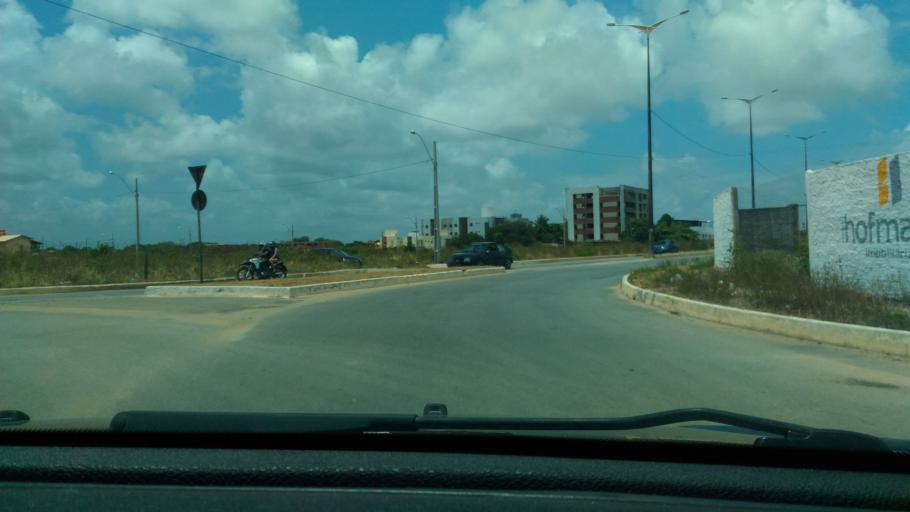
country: BR
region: Paraiba
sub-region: Joao Pessoa
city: Joao Pessoa
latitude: -7.1523
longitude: -34.8166
